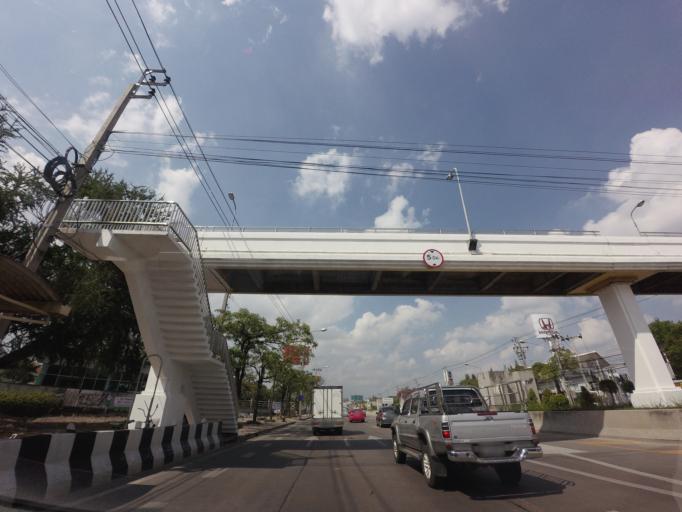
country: TH
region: Bangkok
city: Lat Phrao
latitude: 13.8384
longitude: 100.6009
